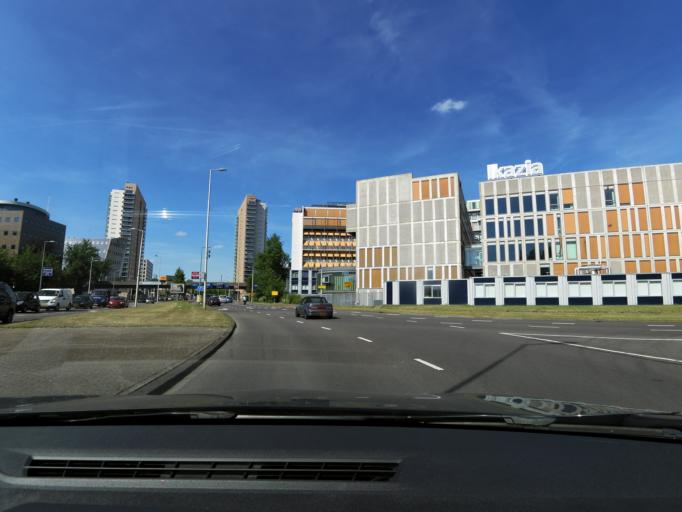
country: NL
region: South Holland
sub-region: Gemeente Rotterdam
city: Rotterdam
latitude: 51.8850
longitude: 4.4920
